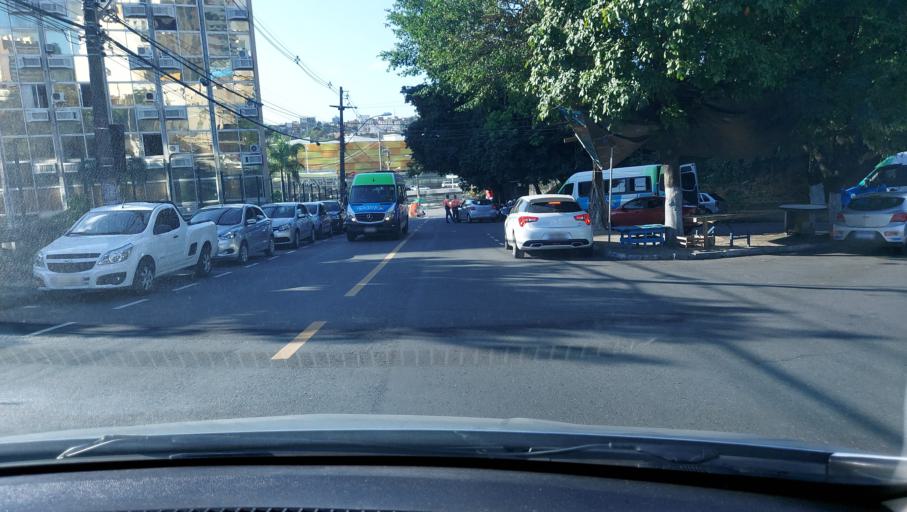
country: BR
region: Bahia
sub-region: Salvador
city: Salvador
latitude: -12.9801
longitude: -38.4624
